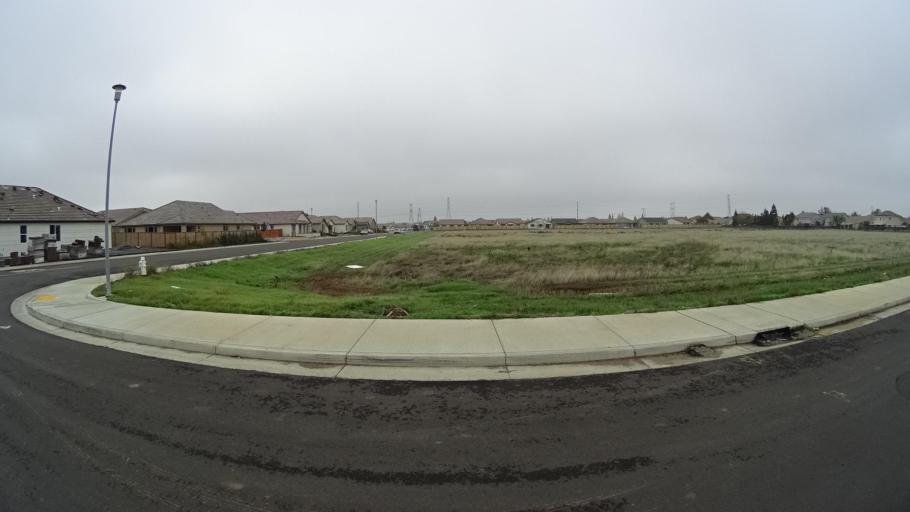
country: US
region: California
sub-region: Sacramento County
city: Elk Grove
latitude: 38.3981
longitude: -121.3441
